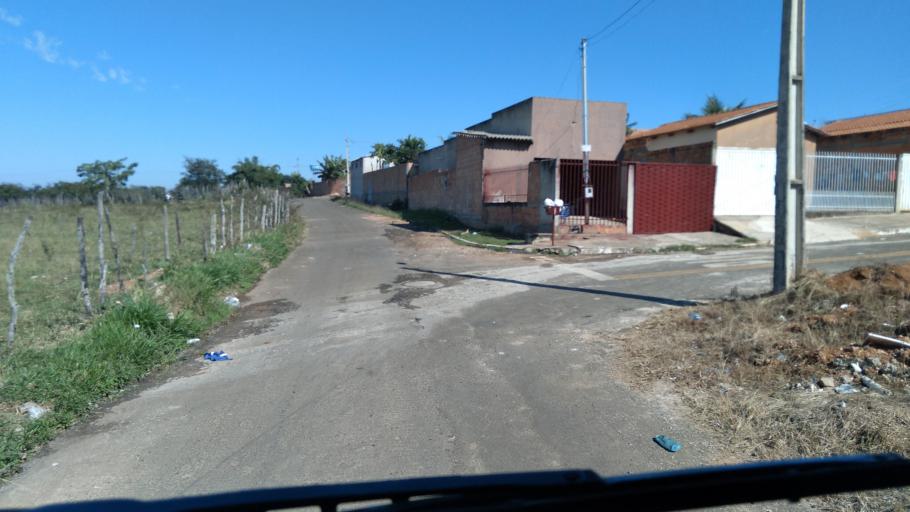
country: BR
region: Goias
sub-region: Mineiros
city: Mineiros
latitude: -17.5783
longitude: -52.5742
